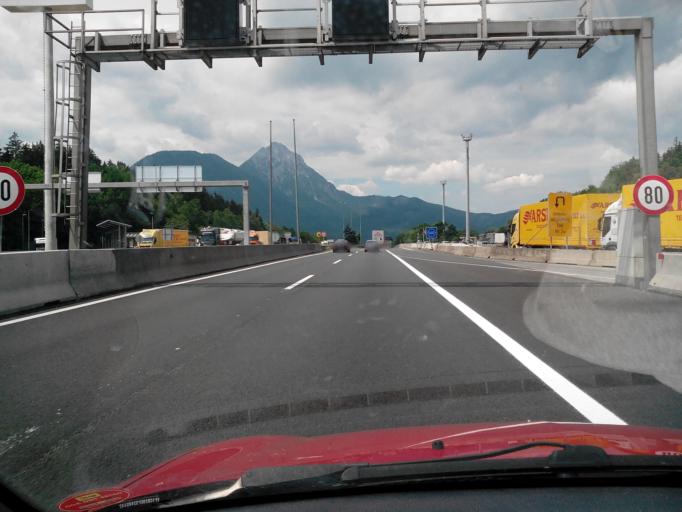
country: DE
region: Bavaria
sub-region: Upper Bavaria
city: Piding
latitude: 47.7685
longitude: 12.9444
